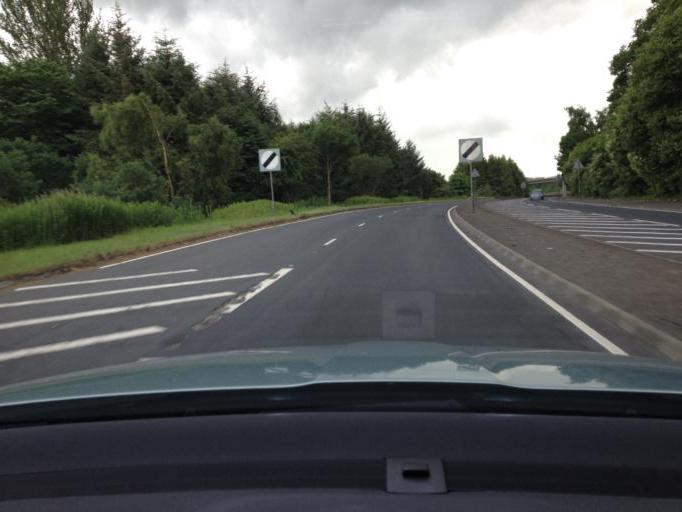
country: GB
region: Scotland
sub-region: Perth and Kinross
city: Perth
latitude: 56.3722
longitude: -3.4233
